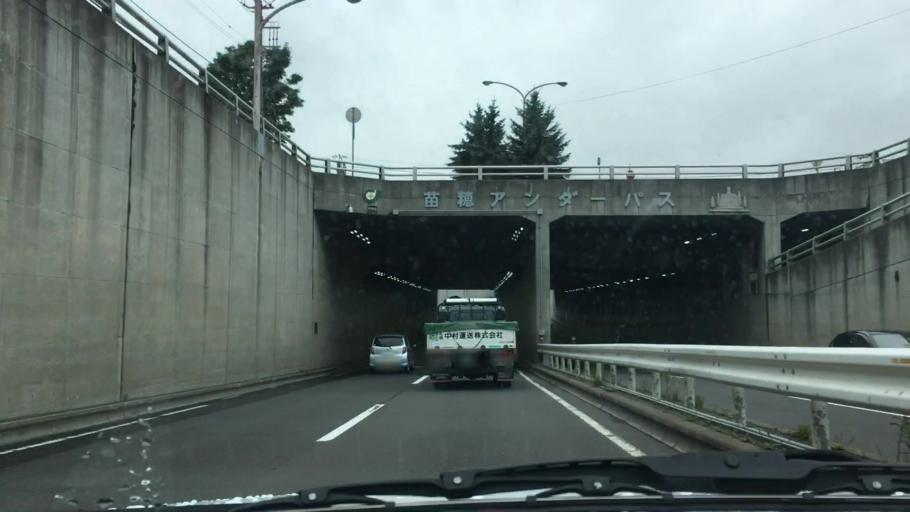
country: JP
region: Hokkaido
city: Sapporo
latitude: 43.0699
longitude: 141.3810
